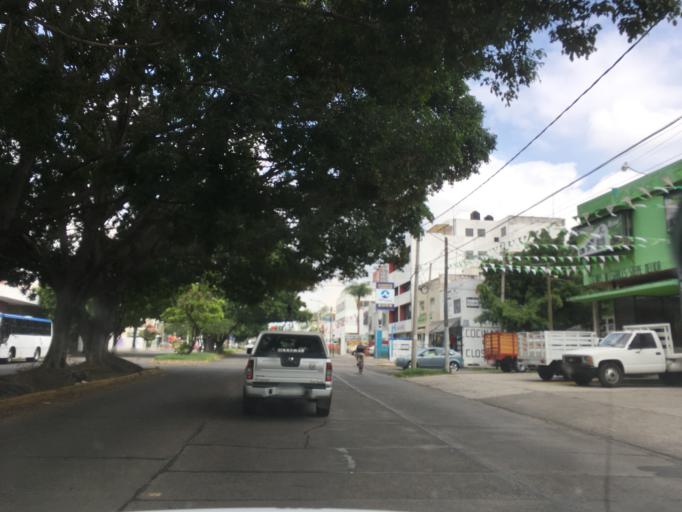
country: MX
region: Jalisco
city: Guadalajara
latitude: 20.6670
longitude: -103.3646
